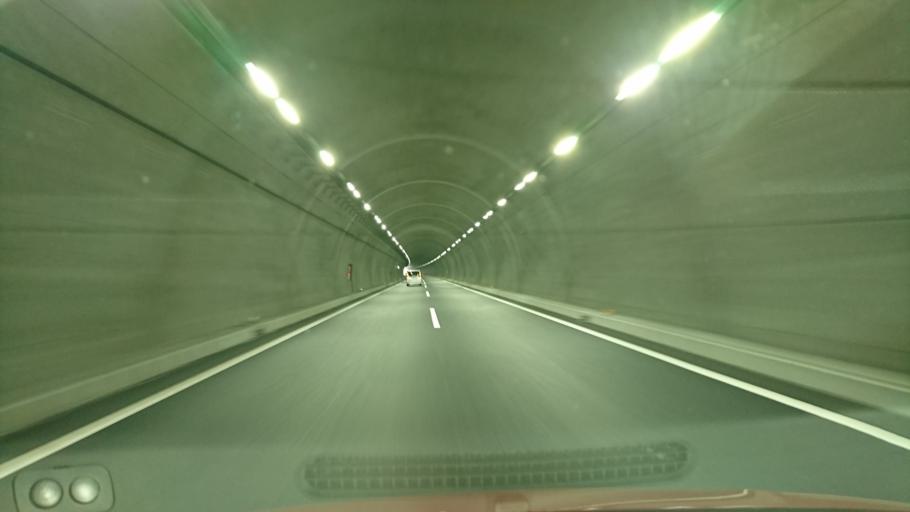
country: JP
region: Hyogo
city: Sandacho
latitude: 34.8540
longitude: 135.2406
